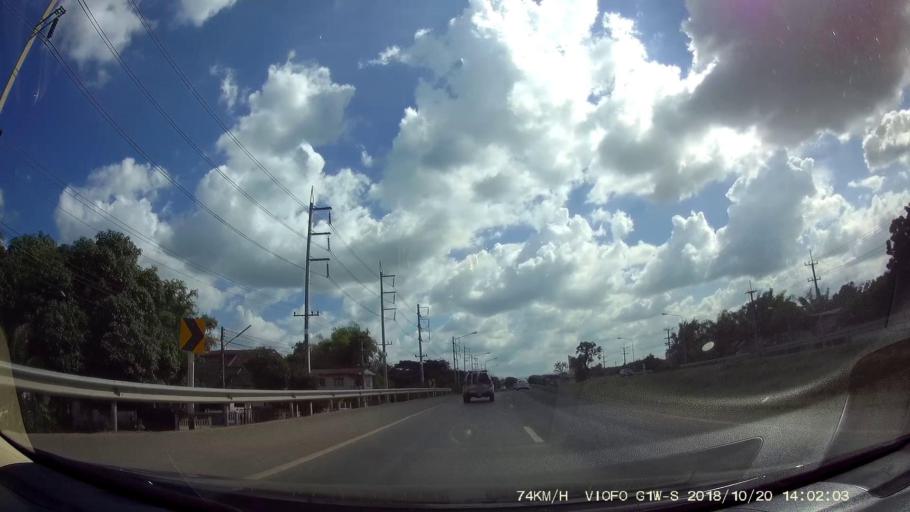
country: TH
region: Khon Kaen
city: Chum Phae
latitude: 16.4959
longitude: 102.1248
